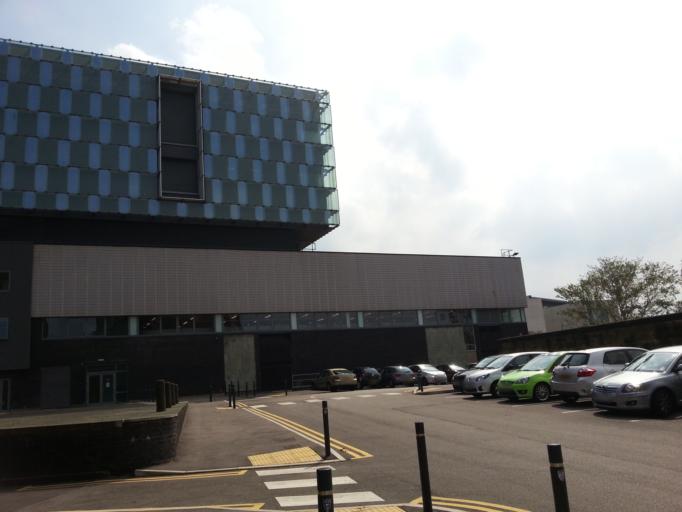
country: GB
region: England
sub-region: Liverpool
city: Liverpool
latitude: 53.4066
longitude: -2.9686
